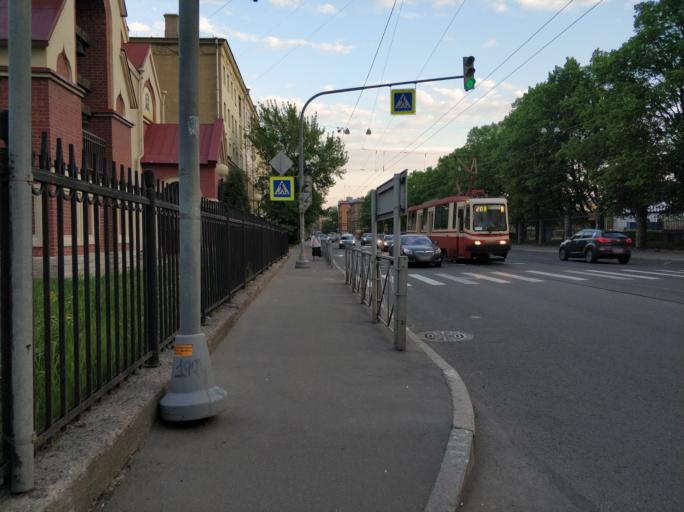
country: RU
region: Leningrad
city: Finlyandskiy
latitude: 59.9655
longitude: 30.3509
